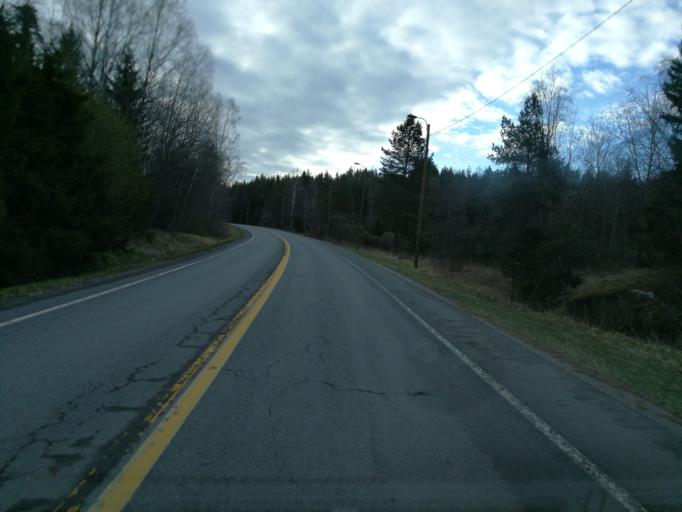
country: FI
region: Varsinais-Suomi
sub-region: Turku
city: Paimio
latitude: 60.4183
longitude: 22.6780
